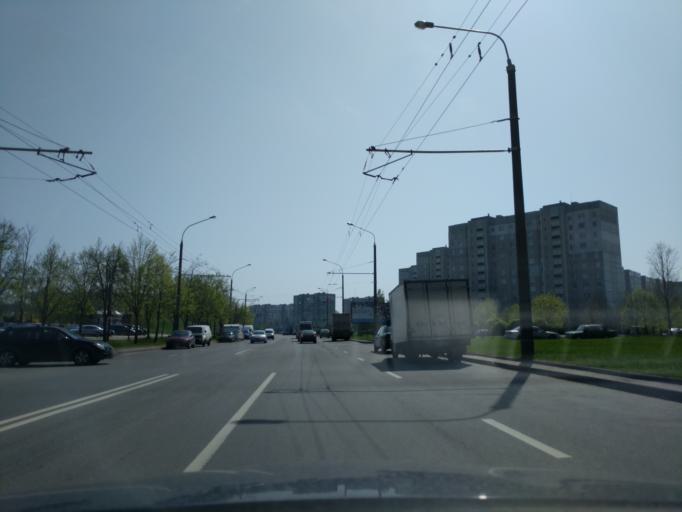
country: BY
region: Minsk
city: Malinovka
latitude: 53.8621
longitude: 27.4583
